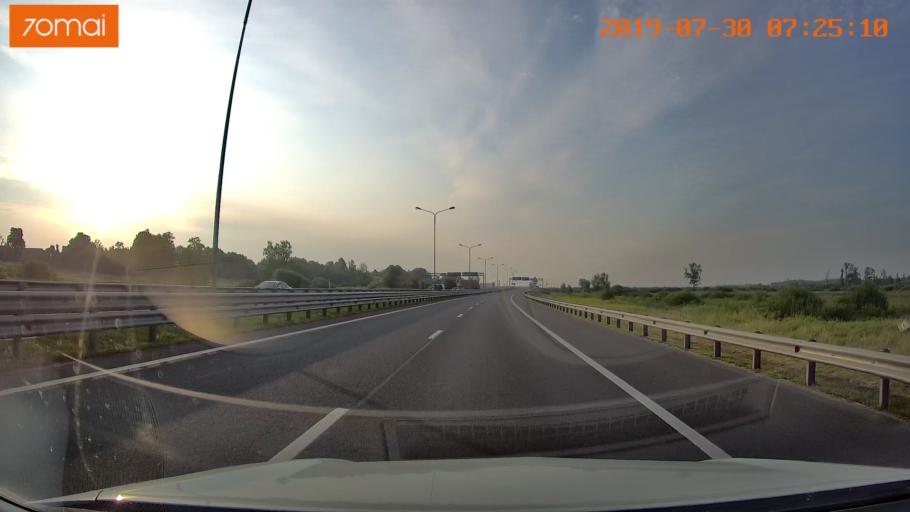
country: RU
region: Kaliningrad
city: Bol'shoe Isakovo
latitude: 54.6885
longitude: 20.8302
